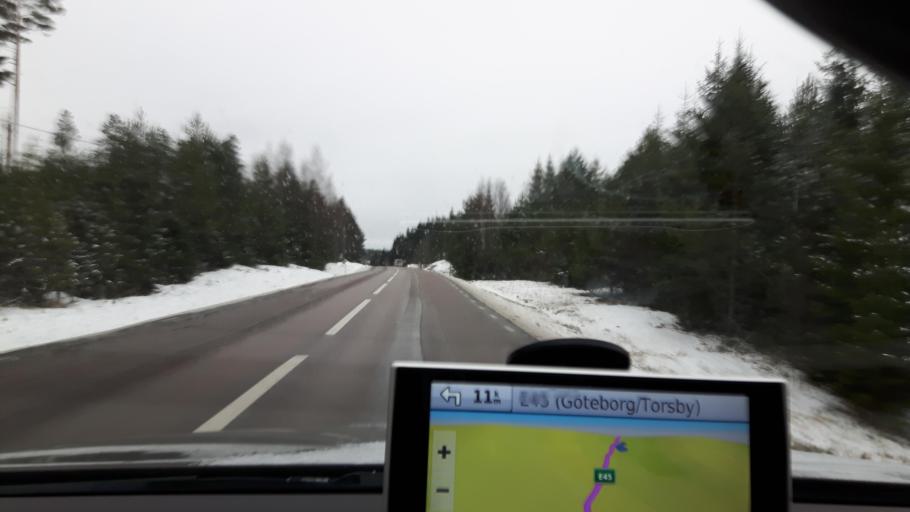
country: SE
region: Vaermland
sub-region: Torsby Kommun
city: Torsby
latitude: 60.3550
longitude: 13.1729
